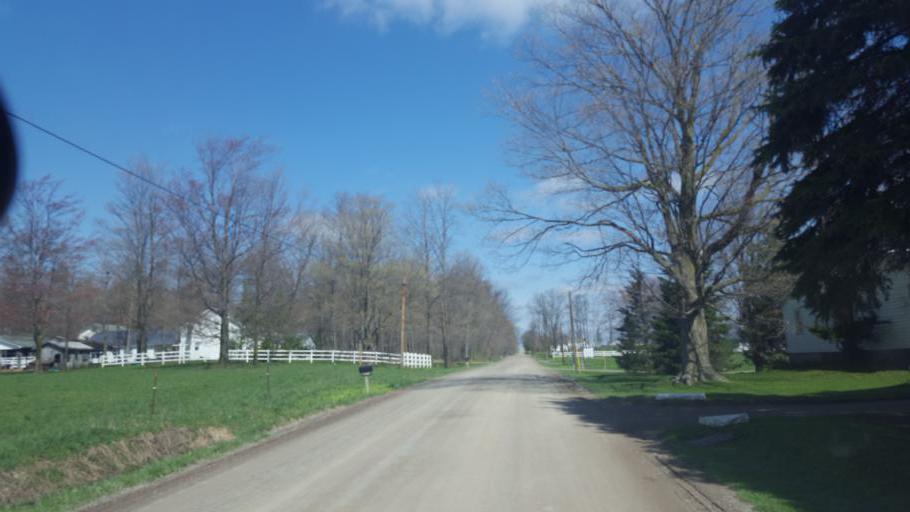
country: US
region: Ohio
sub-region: Geauga County
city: Middlefield
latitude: 41.3907
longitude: -81.0801
